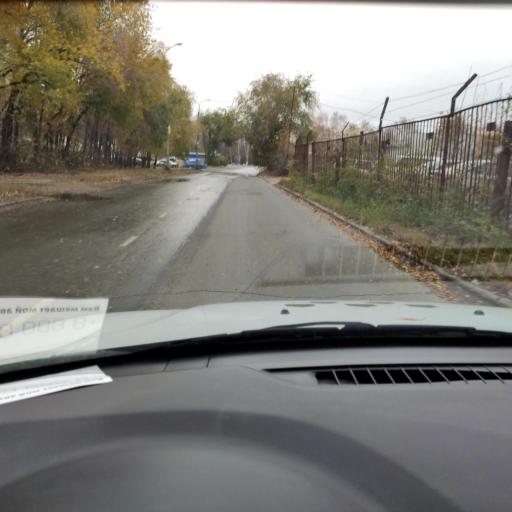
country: RU
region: Samara
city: Tol'yatti
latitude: 53.5529
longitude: 49.3087
